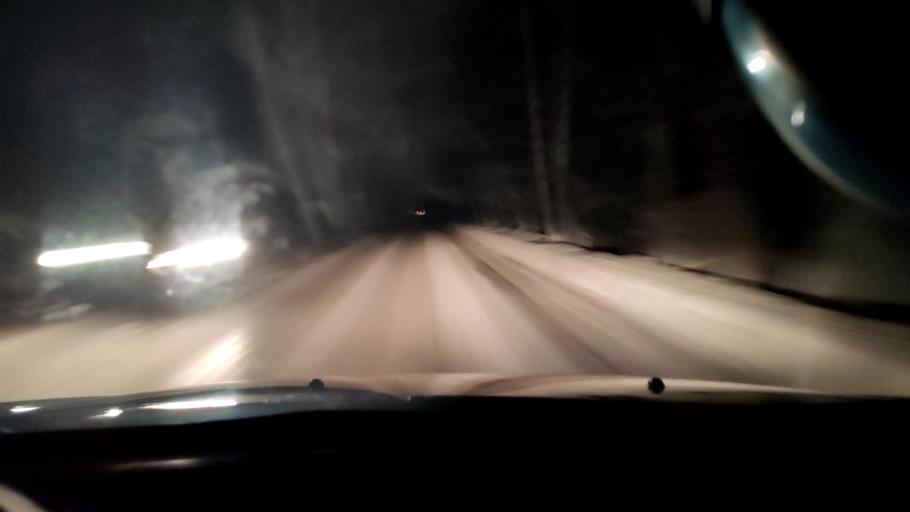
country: RU
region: Perm
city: Overyata
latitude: 58.0260
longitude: 55.9355
